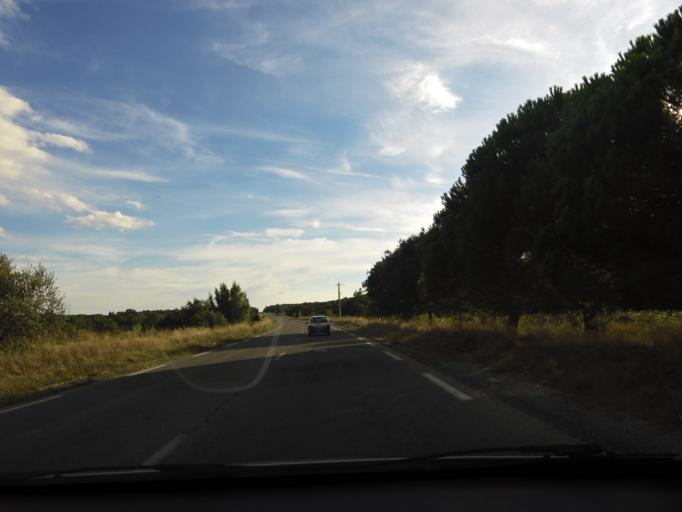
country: FR
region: Languedoc-Roussillon
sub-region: Departement du Gard
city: Quissac
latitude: 43.8862
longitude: 3.9737
